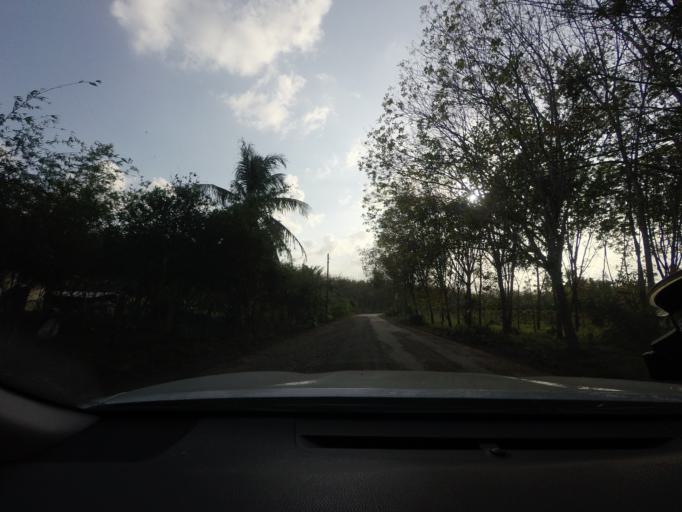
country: TH
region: Pattani
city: Mae Lan
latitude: 6.6160
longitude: 101.2443
